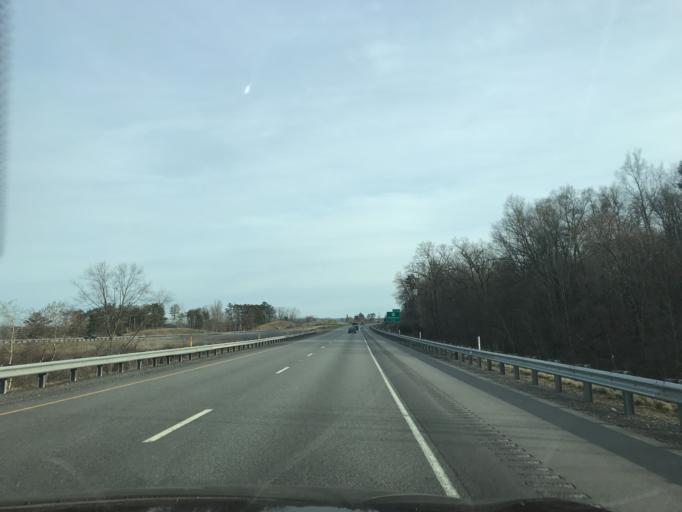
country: US
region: Pennsylvania
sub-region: Lycoming County
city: Muncy
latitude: 41.1396
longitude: -76.8012
